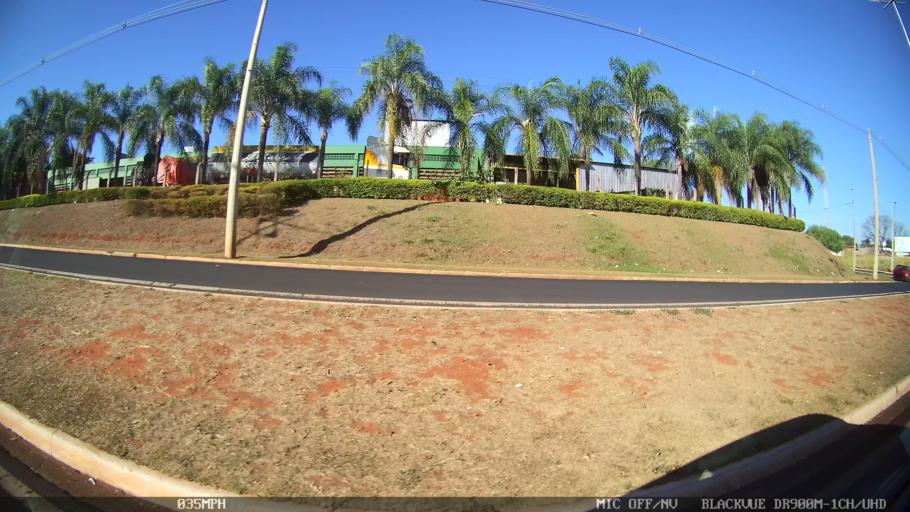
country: BR
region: Sao Paulo
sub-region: Olimpia
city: Olimpia
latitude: -20.7272
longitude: -48.9054
